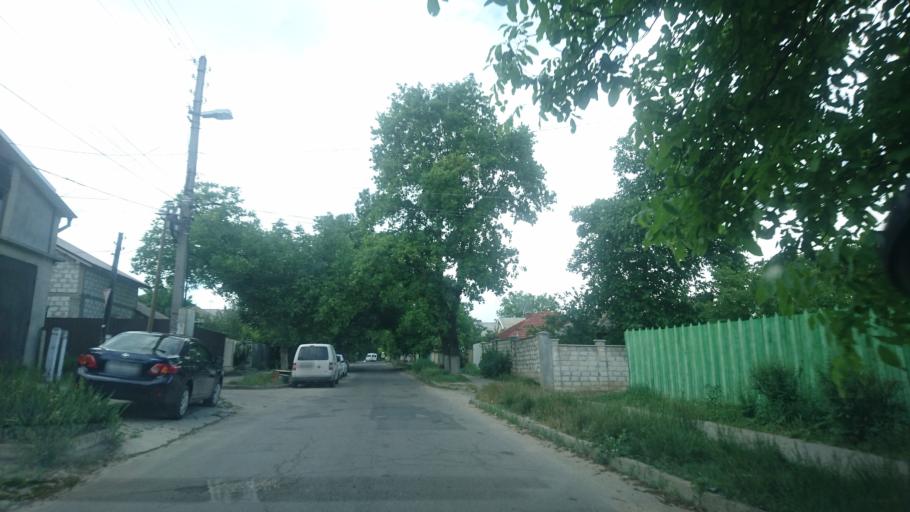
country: MD
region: Chisinau
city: Chisinau
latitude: 47.0504
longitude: 28.8462
